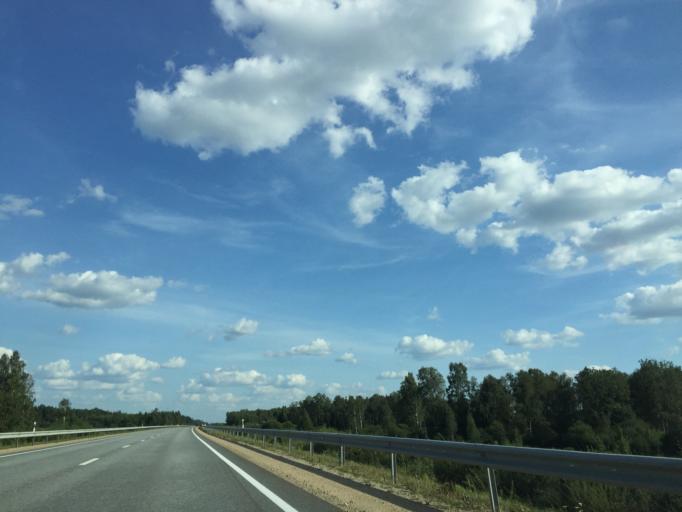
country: LV
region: Koknese
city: Koknese
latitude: 56.6838
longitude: 25.3784
